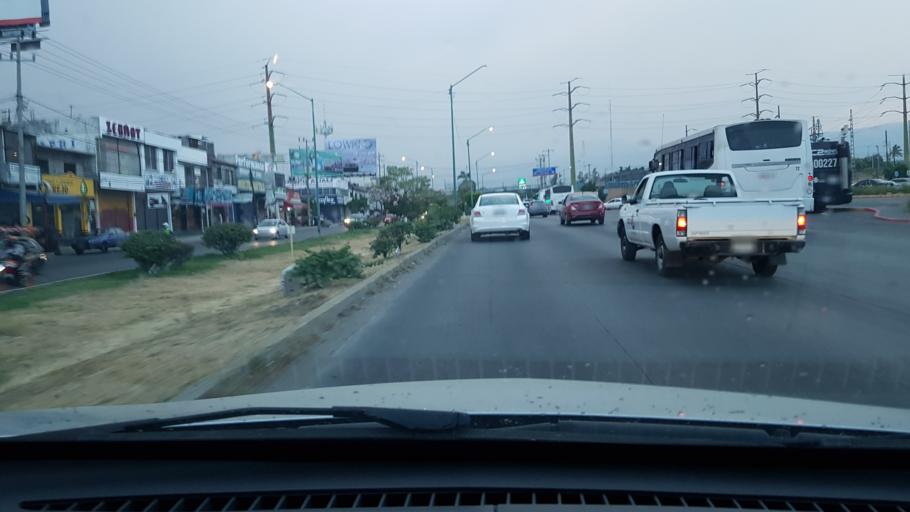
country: MX
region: Morelos
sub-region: Tepoztlan
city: Tetecolala
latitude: 18.9088
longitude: -99.1802
